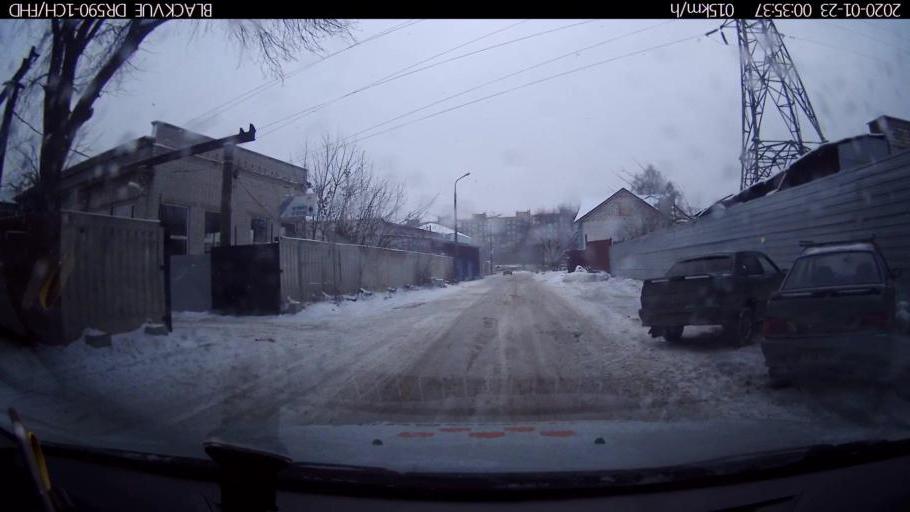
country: RU
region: Nizjnij Novgorod
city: Neklyudovo
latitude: 56.3566
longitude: 43.8532
